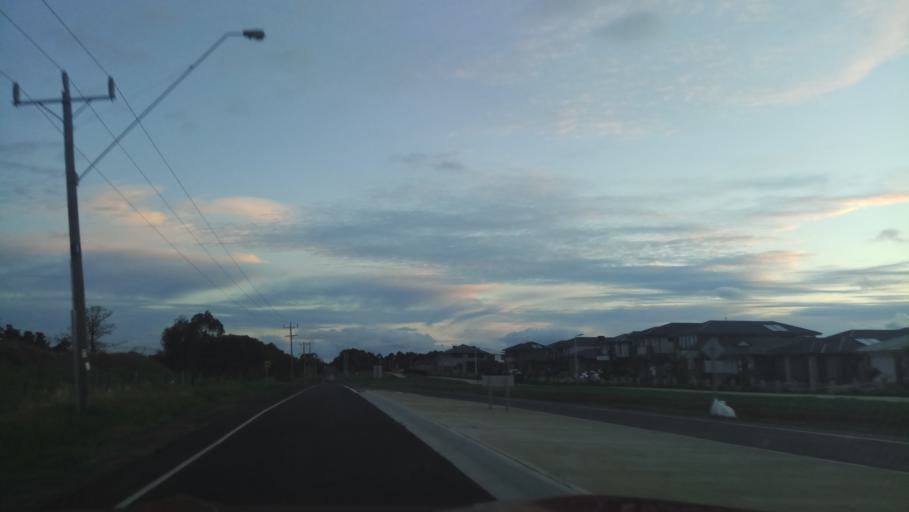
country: AU
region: Victoria
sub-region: Wyndham
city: Point Cook
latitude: -37.9111
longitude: 144.7516
